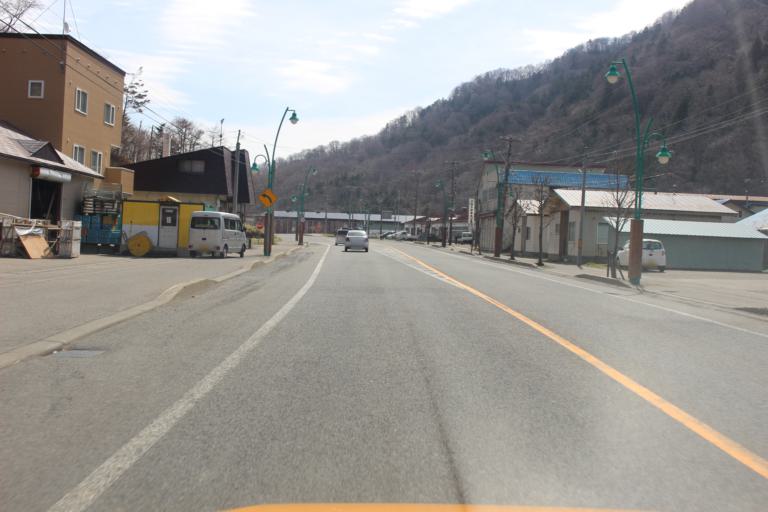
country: JP
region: Hokkaido
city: Kamiiso
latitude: 41.9145
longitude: 140.2280
